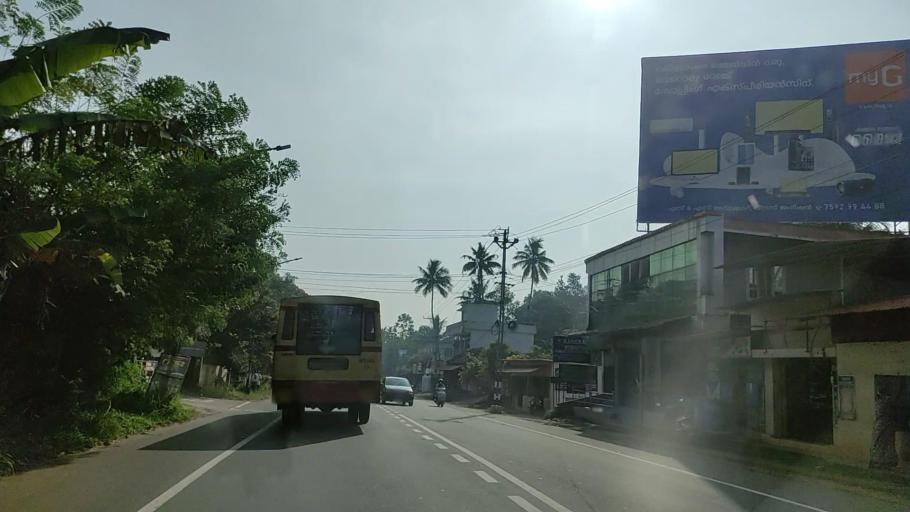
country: IN
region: Kerala
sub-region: Kollam
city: Punalur
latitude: 8.9847
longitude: 76.8038
